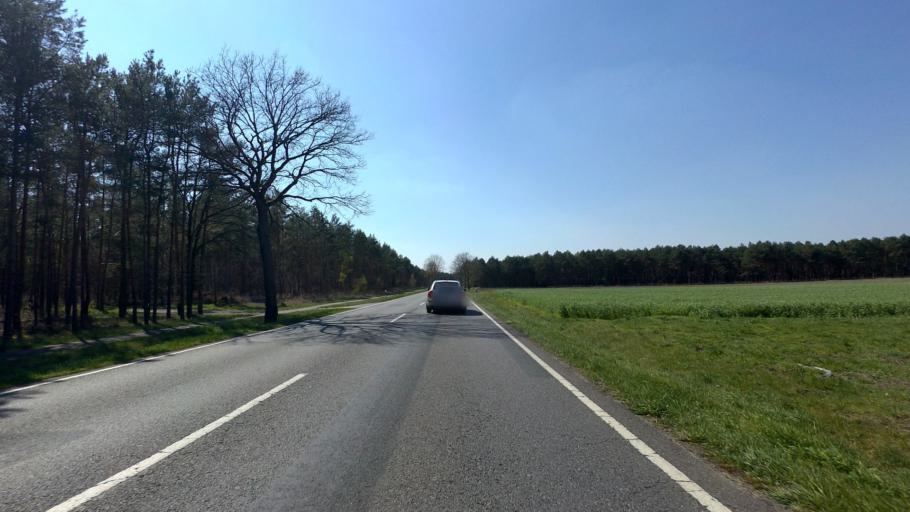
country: DE
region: Lower Saxony
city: Meinersen
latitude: 52.4754
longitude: 10.3985
